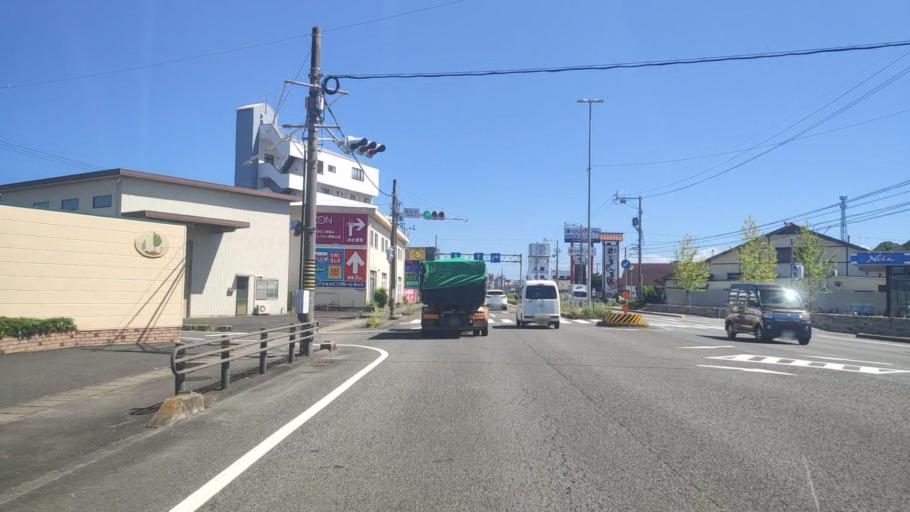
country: JP
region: Mie
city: Tsu-shi
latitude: 34.6999
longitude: 136.5081
